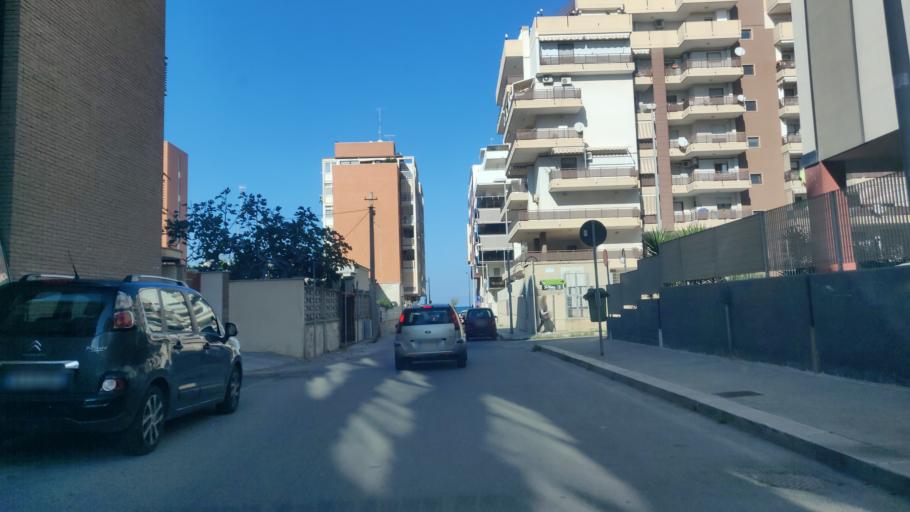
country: IT
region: Apulia
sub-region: Provincia di Bari
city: San Paolo
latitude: 41.1381
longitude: 16.8155
